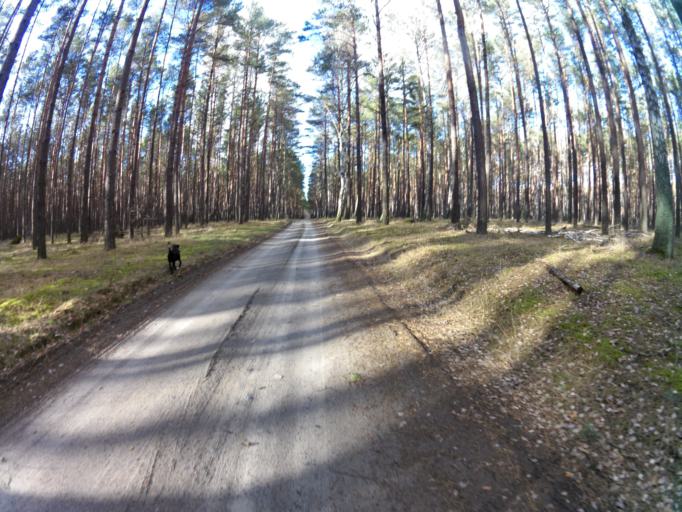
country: PL
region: West Pomeranian Voivodeship
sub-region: Powiat mysliborski
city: Debno
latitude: 52.7969
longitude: 14.7479
